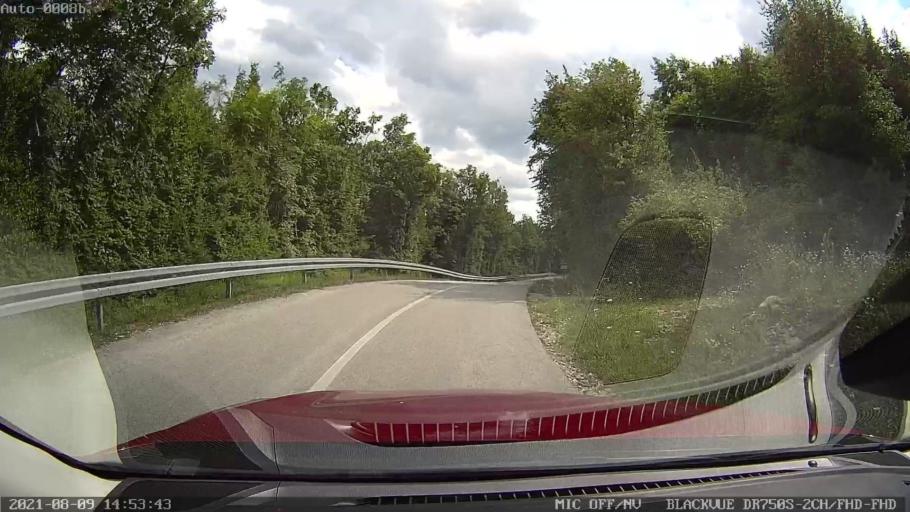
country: HR
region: Istarska
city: Pazin
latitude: 45.2829
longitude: 14.0757
